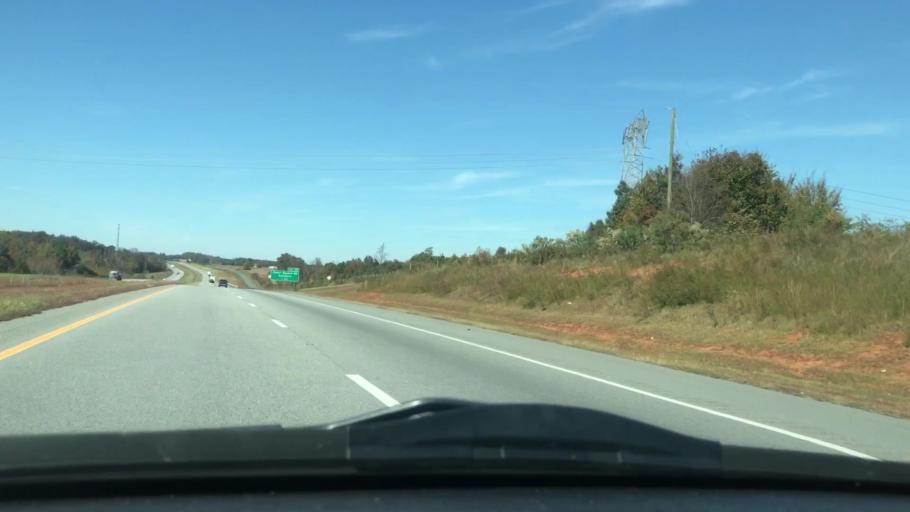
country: US
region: North Carolina
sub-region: Randolph County
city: Randleman
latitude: 35.8583
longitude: -79.8848
